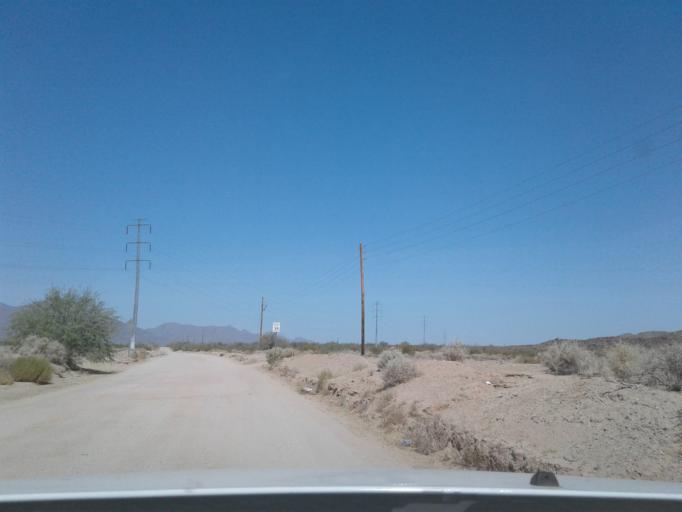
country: US
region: Arizona
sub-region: Maricopa County
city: Laveen
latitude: 33.2903
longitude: -112.1340
